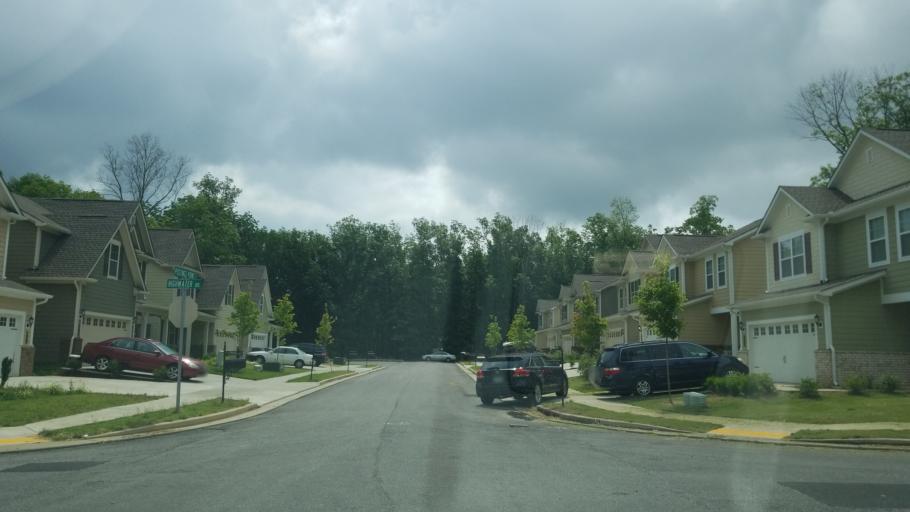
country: US
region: Tennessee
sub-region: Rutherford County
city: La Vergne
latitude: 36.0575
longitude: -86.6018
